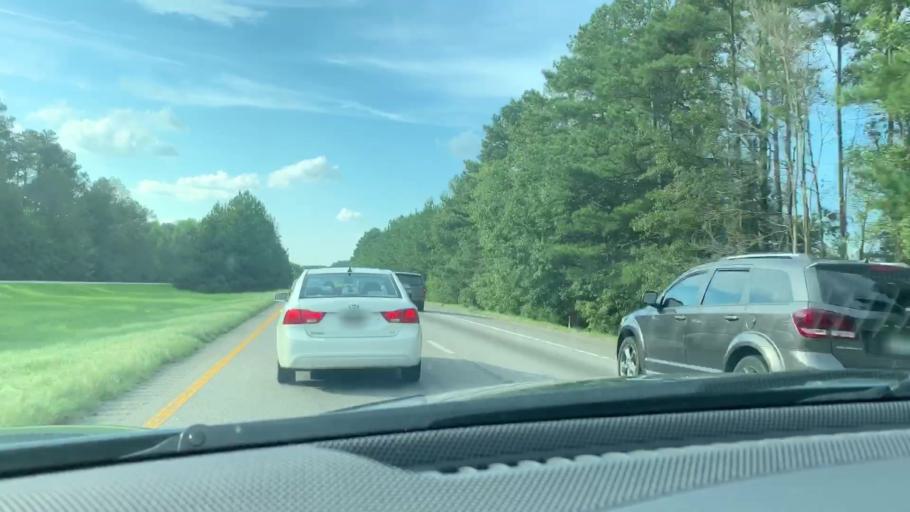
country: US
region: South Carolina
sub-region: Orangeburg County
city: Brookdale
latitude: 33.4438
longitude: -80.7111
